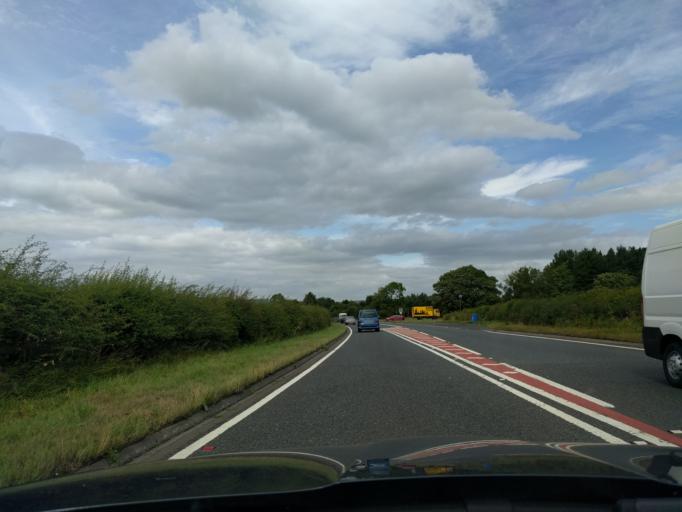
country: GB
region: England
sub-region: Northumberland
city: Felton
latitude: 55.2645
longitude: -1.7118
